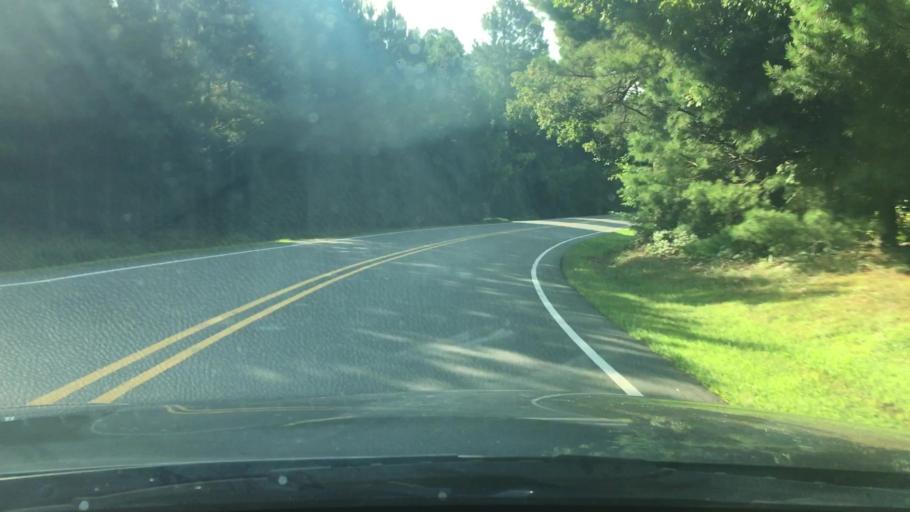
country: US
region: North Carolina
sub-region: Caswell County
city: Yanceyville
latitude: 36.2649
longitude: -79.3410
